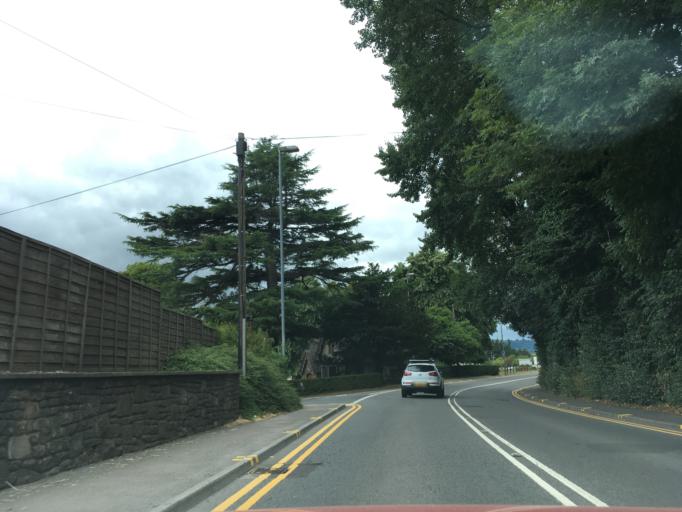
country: GB
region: Wales
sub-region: Monmouthshire
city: Abergavenny
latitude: 51.8254
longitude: -3.0322
